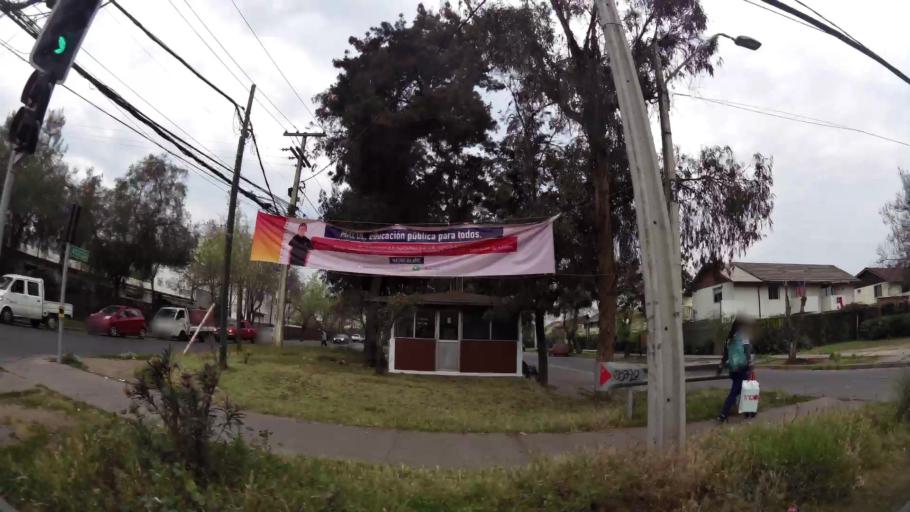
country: CL
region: Santiago Metropolitan
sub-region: Provincia de Santiago
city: Villa Presidente Frei, Nunoa, Santiago, Chile
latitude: -33.4745
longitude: -70.6134
